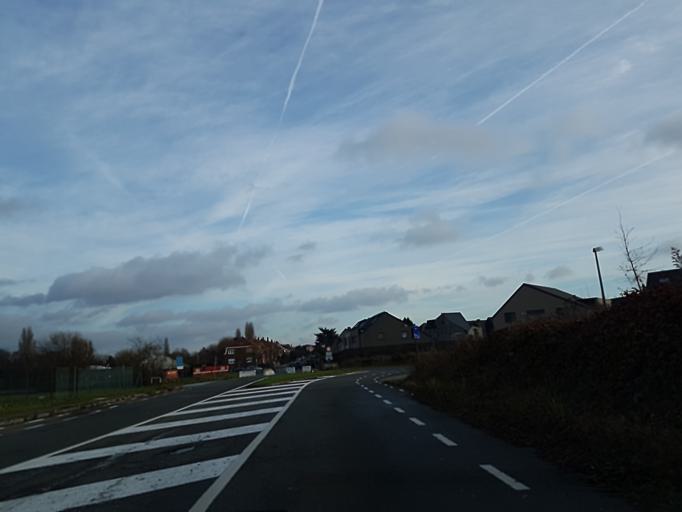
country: BE
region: Flanders
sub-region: Provincie Vlaams-Brabant
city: Diegem
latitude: 50.8695
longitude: 4.4325
